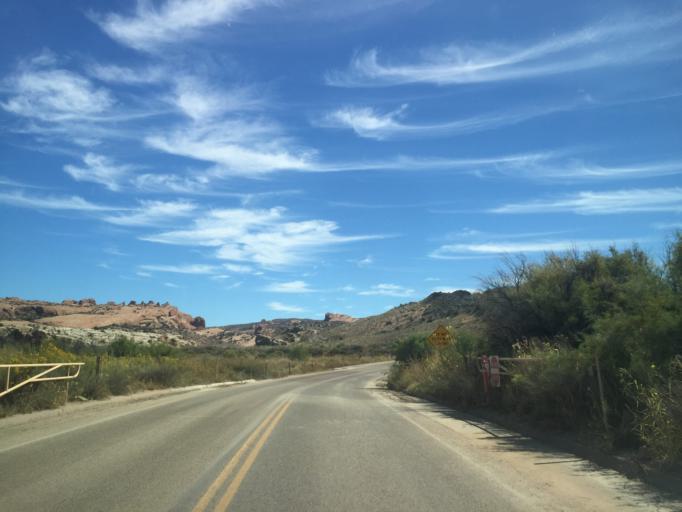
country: US
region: Utah
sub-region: Grand County
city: Moab
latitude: 38.7351
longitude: -109.5200
